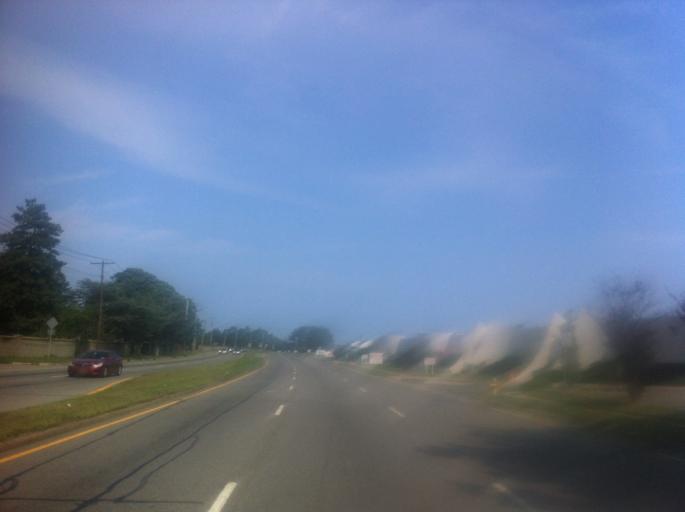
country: US
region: New York
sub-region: Suffolk County
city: East Farmingdale
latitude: 40.7176
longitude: -73.4054
